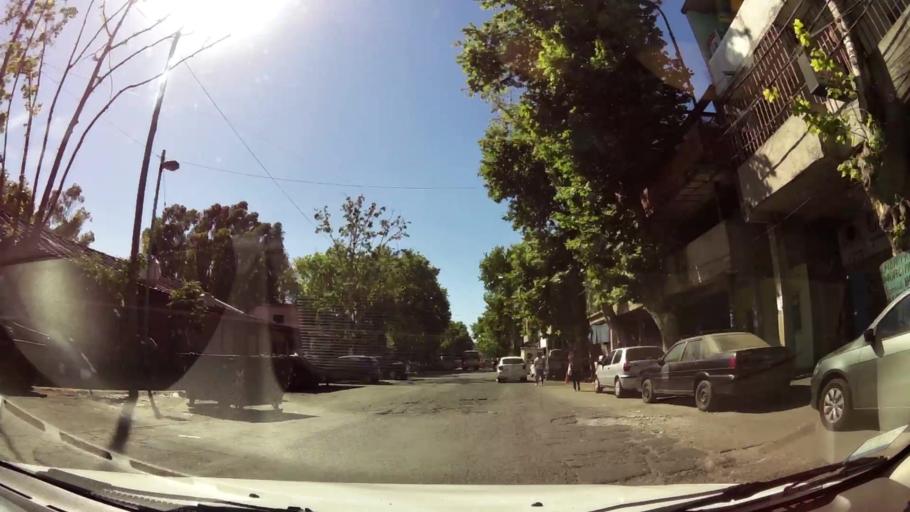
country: AR
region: Buenos Aires F.D.
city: Retiro
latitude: -34.5834
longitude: -58.3771
